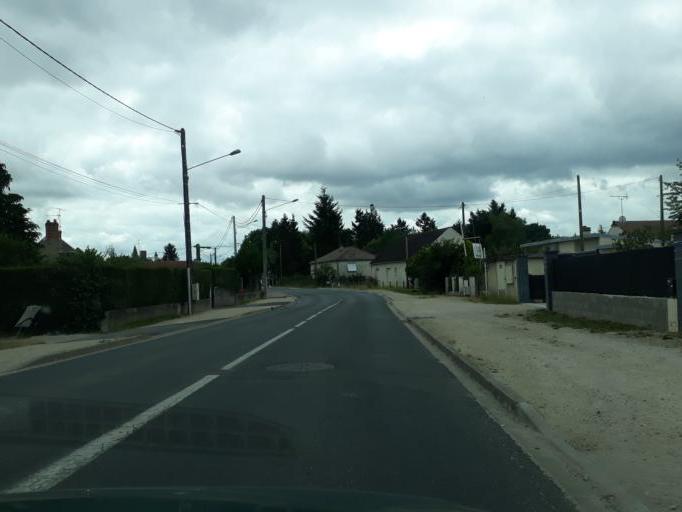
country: FR
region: Centre
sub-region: Departement du Loiret
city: Sandillon
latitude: 47.8513
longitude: 2.0207
